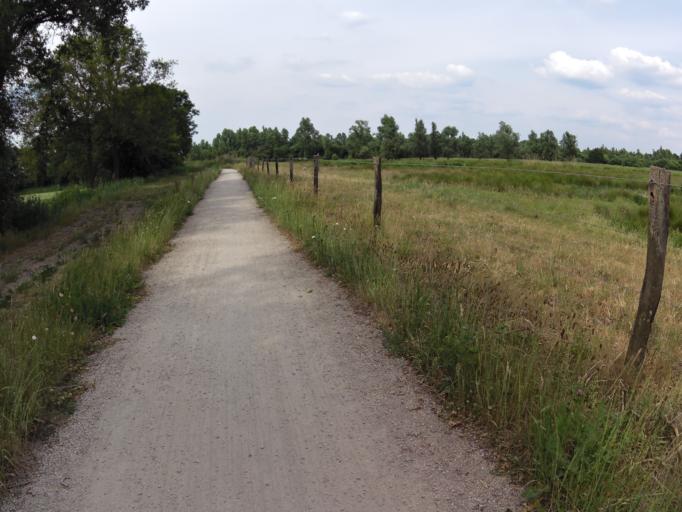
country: NL
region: North Brabant
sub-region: Gemeente Oirschot
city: Oirschot
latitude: 51.5366
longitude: 5.2623
